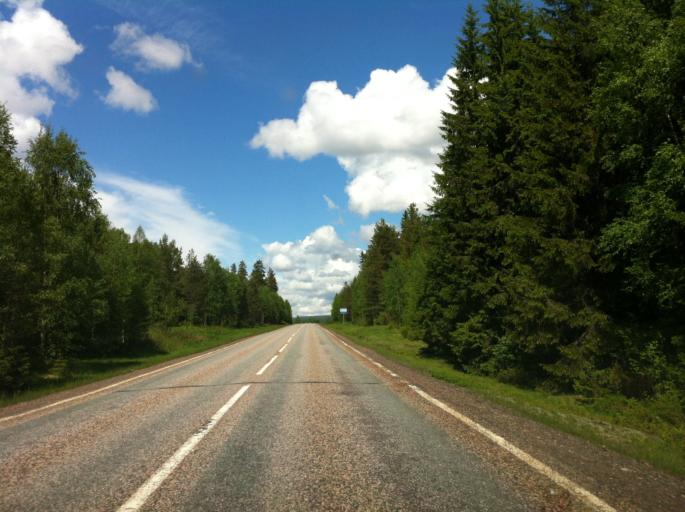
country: SE
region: Dalarna
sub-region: Malung-Saelens kommun
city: Malung
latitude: 61.0139
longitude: 13.3349
